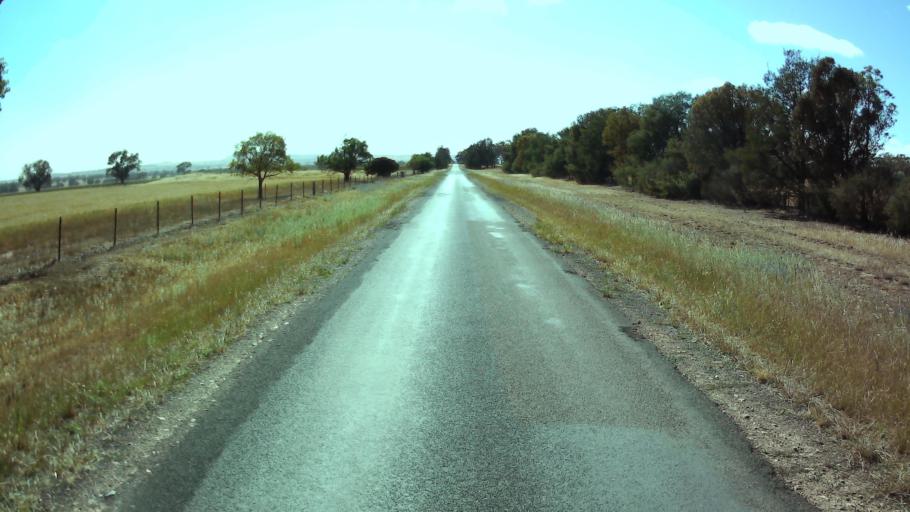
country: AU
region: New South Wales
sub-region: Weddin
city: Grenfell
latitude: -34.0627
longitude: 148.2820
